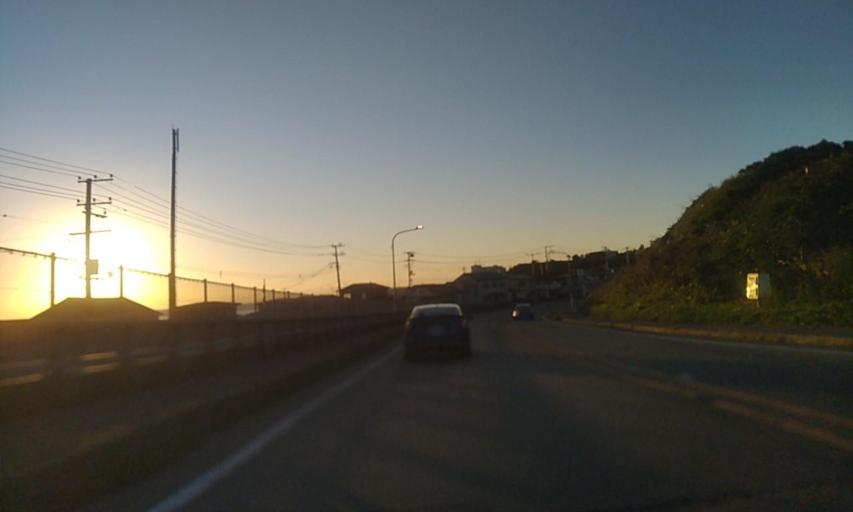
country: JP
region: Hokkaido
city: Shizunai-furukawacho
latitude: 42.1584
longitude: 142.7832
